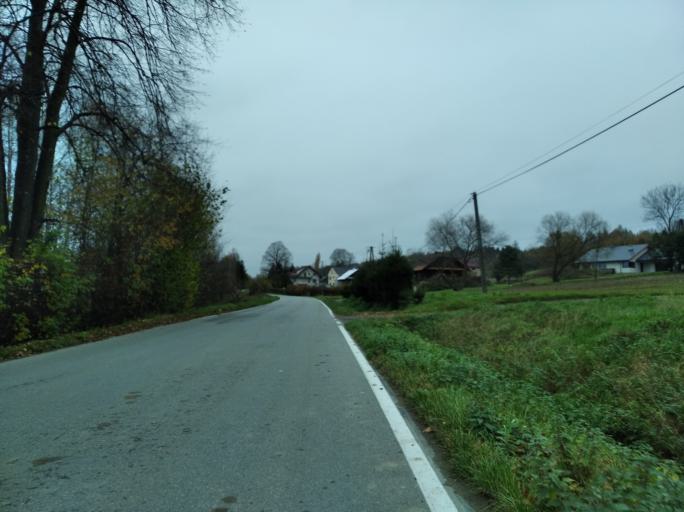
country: PL
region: Subcarpathian Voivodeship
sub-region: Powiat krosnienski
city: Leki
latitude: 49.8164
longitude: 21.6517
